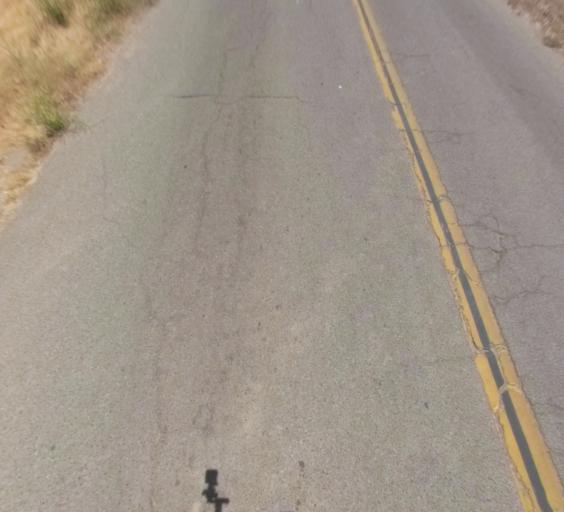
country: US
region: California
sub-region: Madera County
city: Parksdale
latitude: 36.9526
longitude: -120.0204
